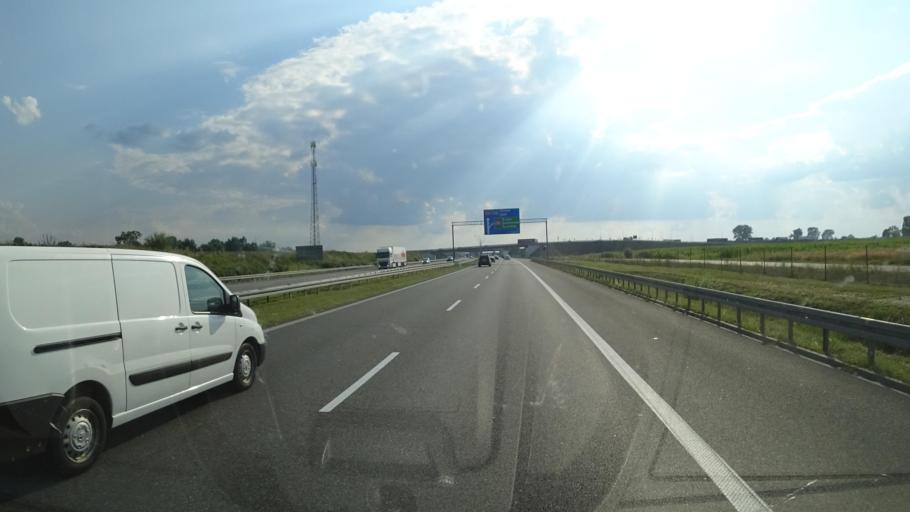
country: PL
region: Masovian Voivodeship
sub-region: Powiat zyrardowski
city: Wiskitki
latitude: 52.0933
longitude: 20.3724
